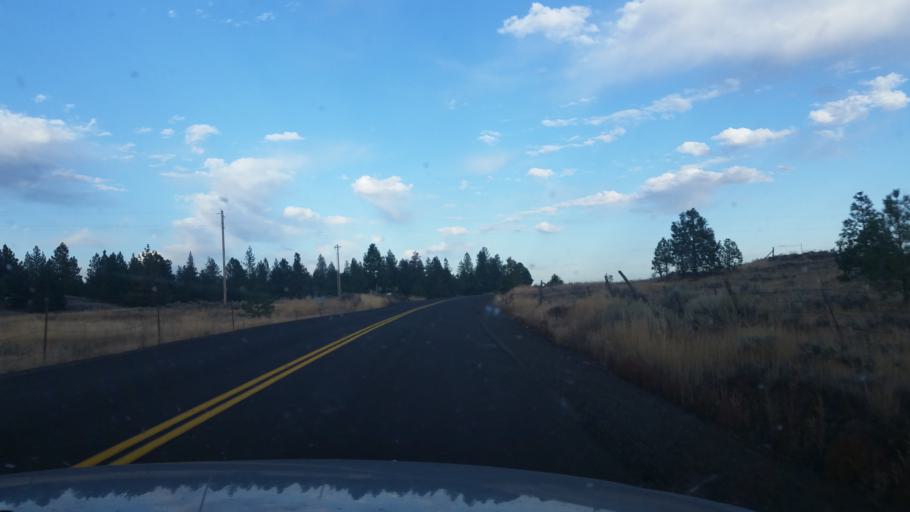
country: US
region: Washington
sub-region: Spokane County
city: Medical Lake
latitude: 47.4531
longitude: -117.8128
